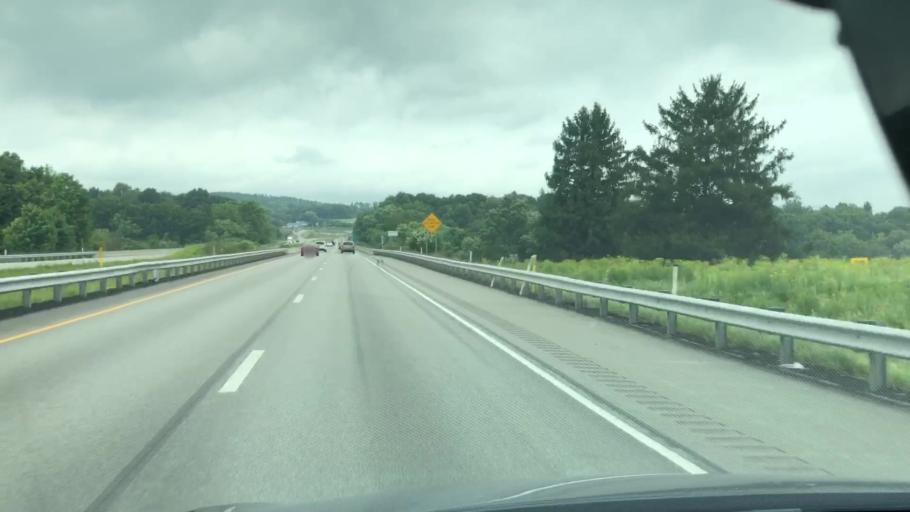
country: US
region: Pennsylvania
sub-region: Butler County
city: Zelienople
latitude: 40.8004
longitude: -80.1196
